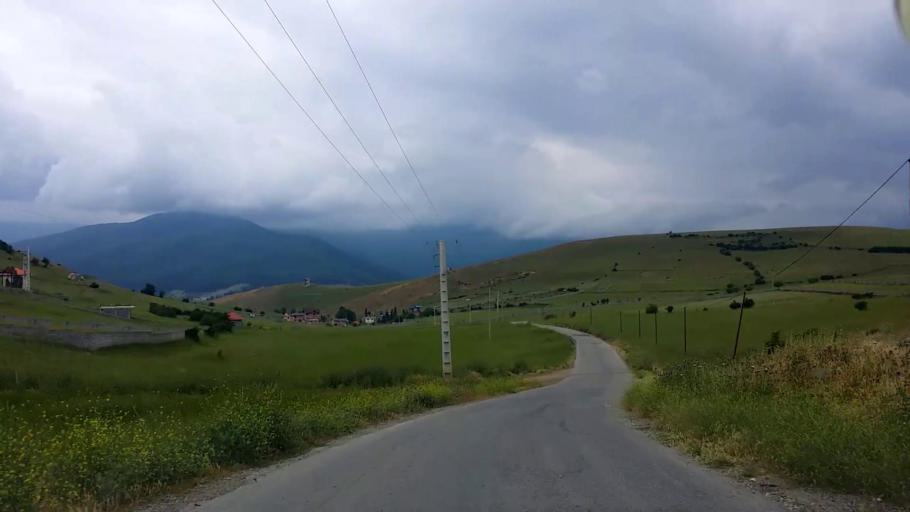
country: IR
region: Mazandaran
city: Chalus
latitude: 36.5270
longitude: 51.2676
